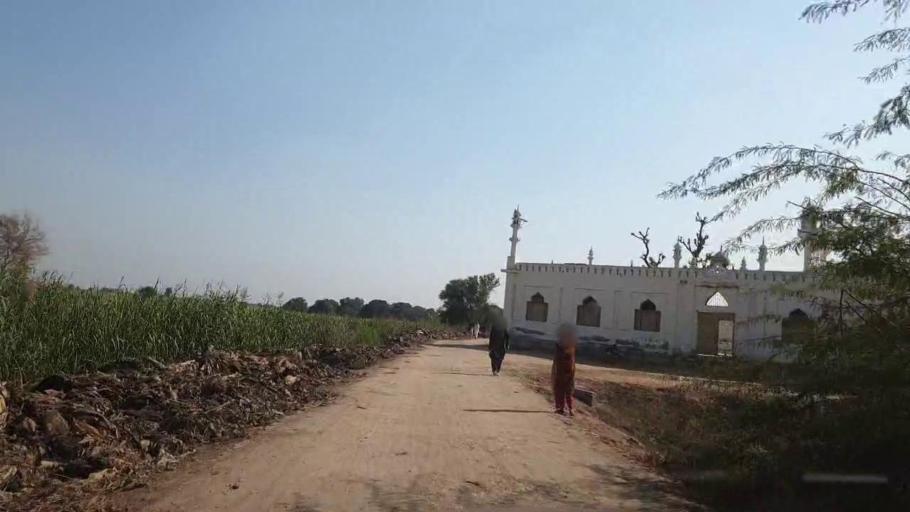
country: PK
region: Sindh
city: Tando Allahyar
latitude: 25.5847
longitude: 68.7530
